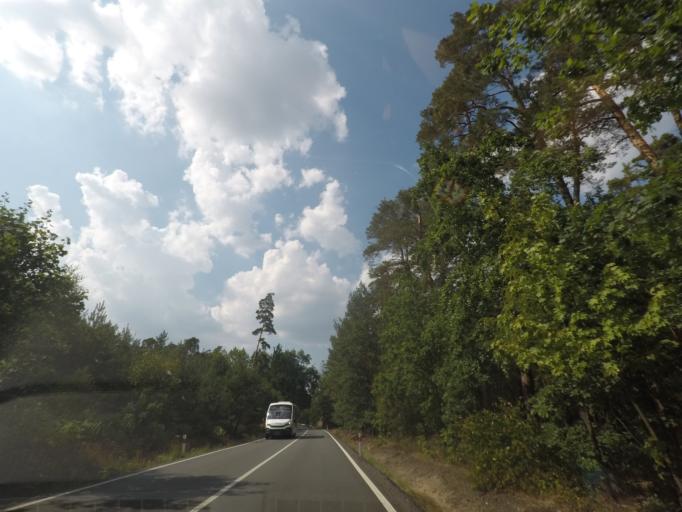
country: CZ
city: Borohradek
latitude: 50.1105
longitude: 16.0763
